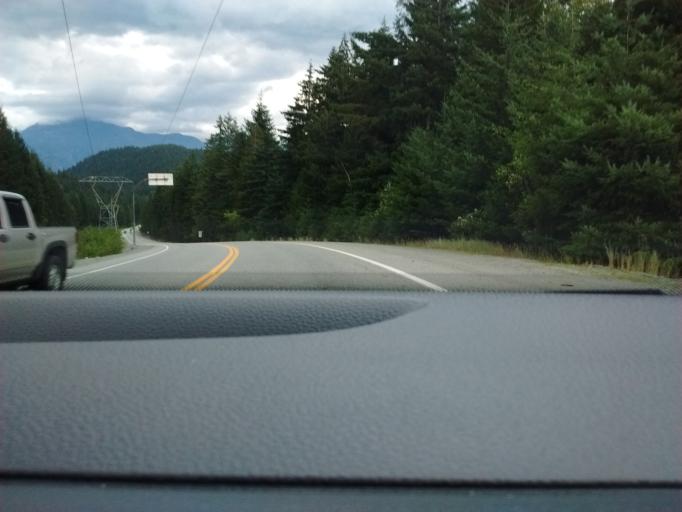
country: CA
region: British Columbia
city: Pemberton
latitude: 50.2935
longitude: -122.8303
